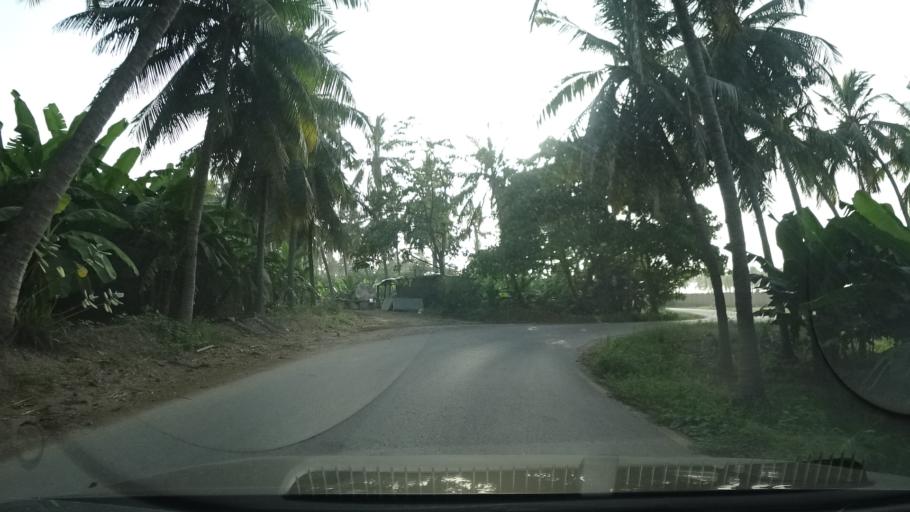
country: OM
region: Zufar
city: Salalah
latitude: 17.0179
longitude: 54.1439
